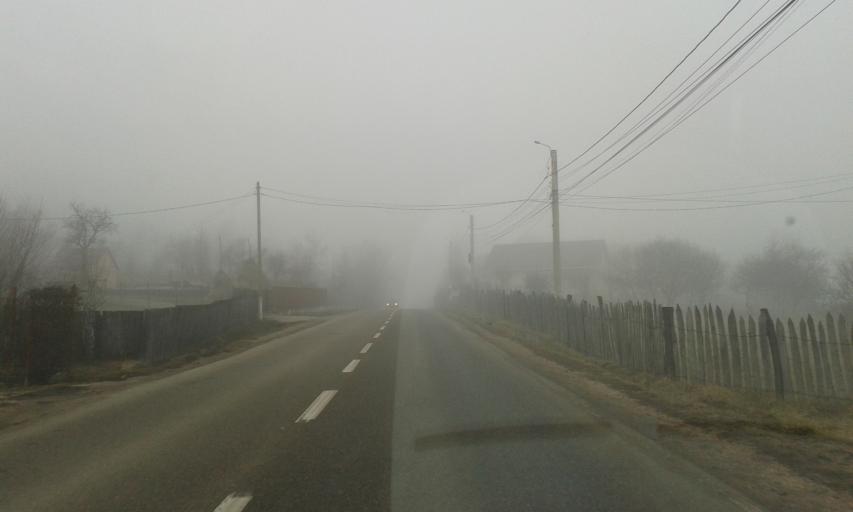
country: RO
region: Hunedoara
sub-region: Comuna Aninoasa
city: Iscroni
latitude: 45.3765
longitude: 23.3130
